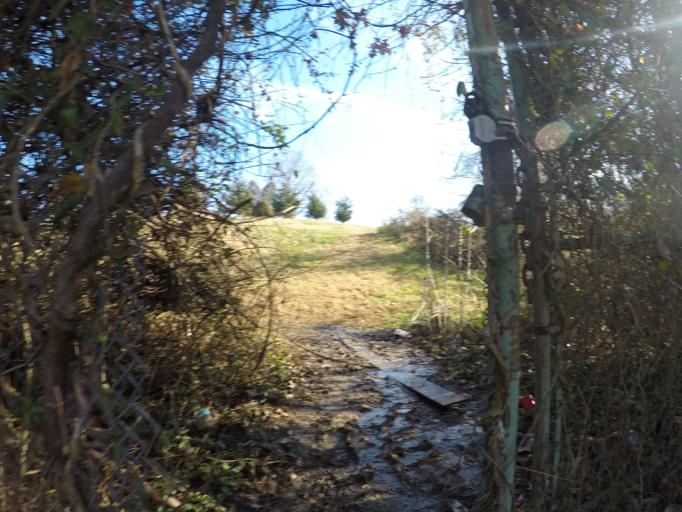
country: US
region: West Virginia
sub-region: Cabell County
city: Huntington
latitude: 38.4083
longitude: -82.4184
